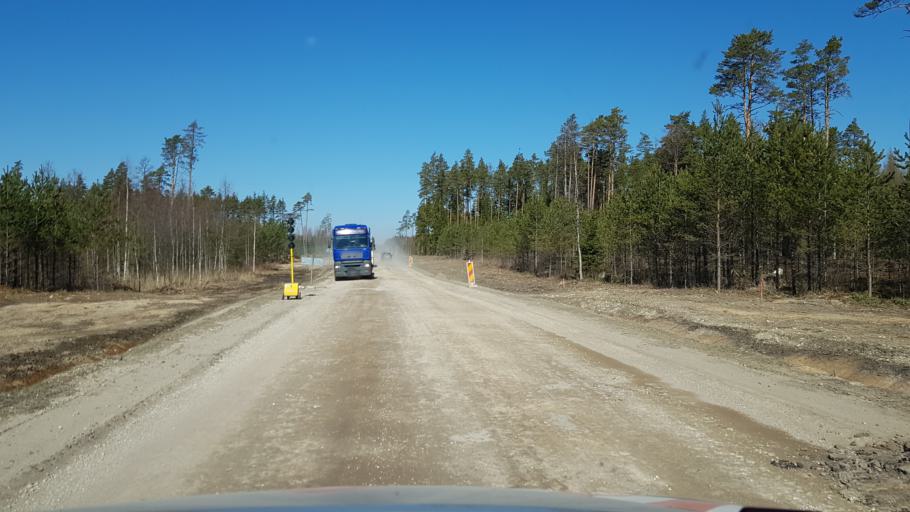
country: EE
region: Jogevamaa
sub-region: Mustvee linn
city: Mustvee
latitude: 59.0445
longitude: 26.6617
